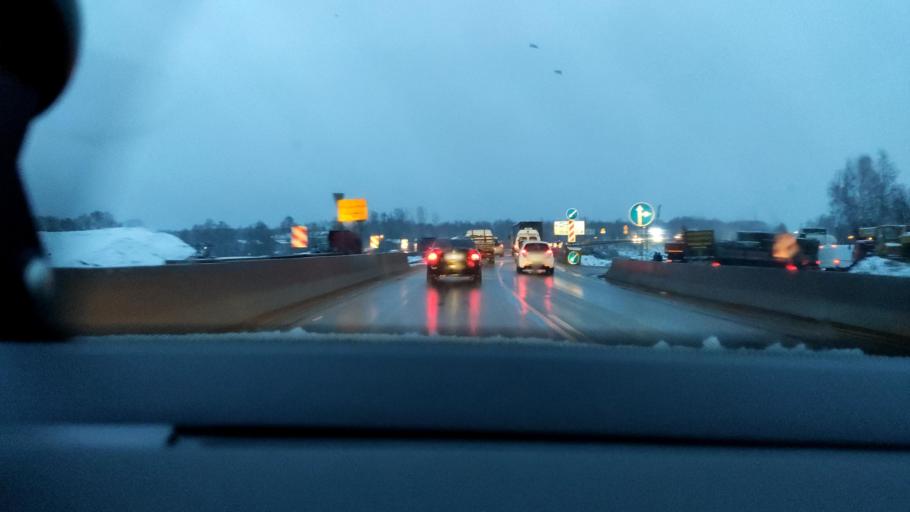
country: RU
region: Moskovskaya
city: Kubinka
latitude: 55.5688
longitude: 36.6972
